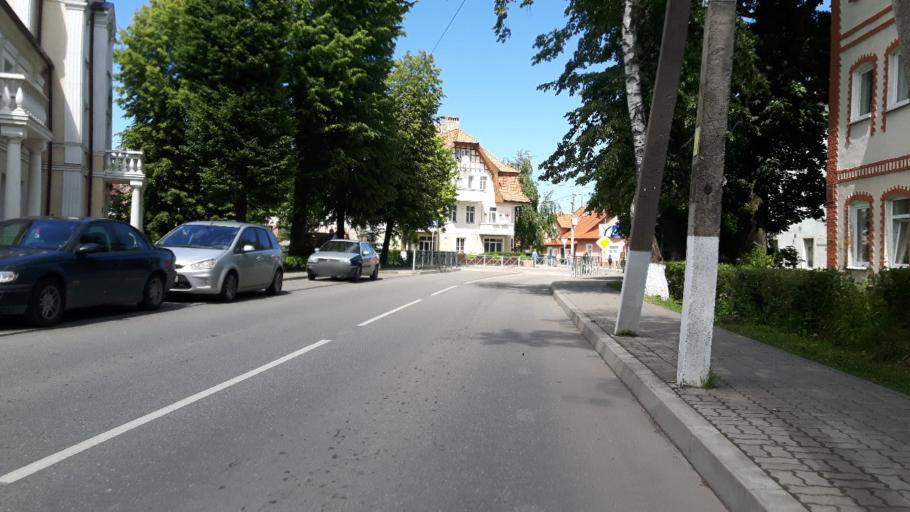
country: RU
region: Kaliningrad
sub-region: Zelenogradskiy Rayon
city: Zelenogradsk
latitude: 54.9579
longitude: 20.4717
